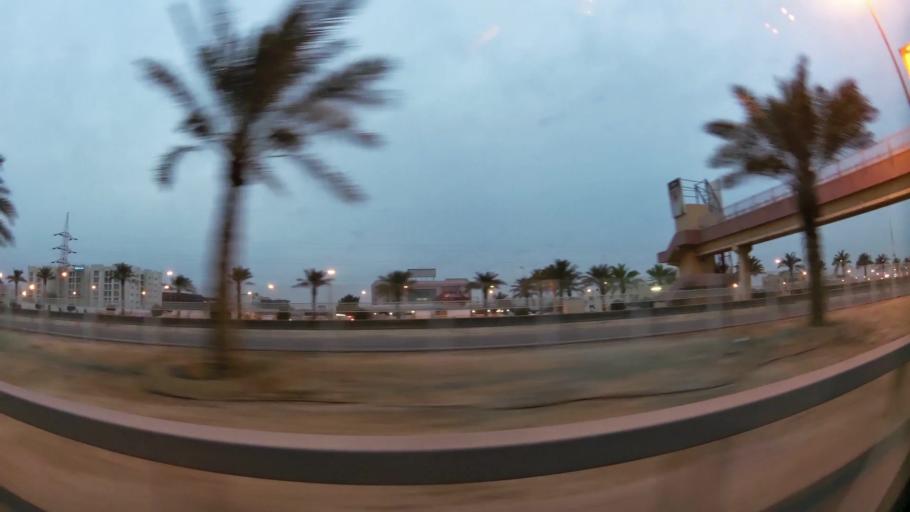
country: BH
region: Northern
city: Madinat `Isa
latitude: 26.1591
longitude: 50.5653
